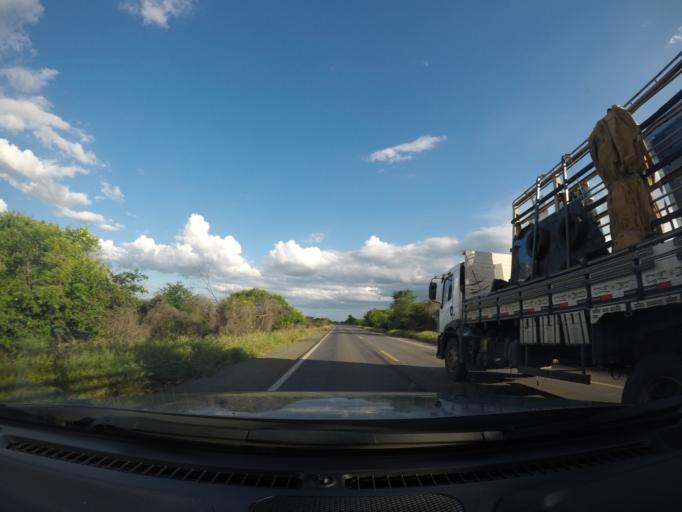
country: BR
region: Bahia
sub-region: Oliveira Dos Brejinhos
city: Beira Rio
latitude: -12.2108
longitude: -42.8023
